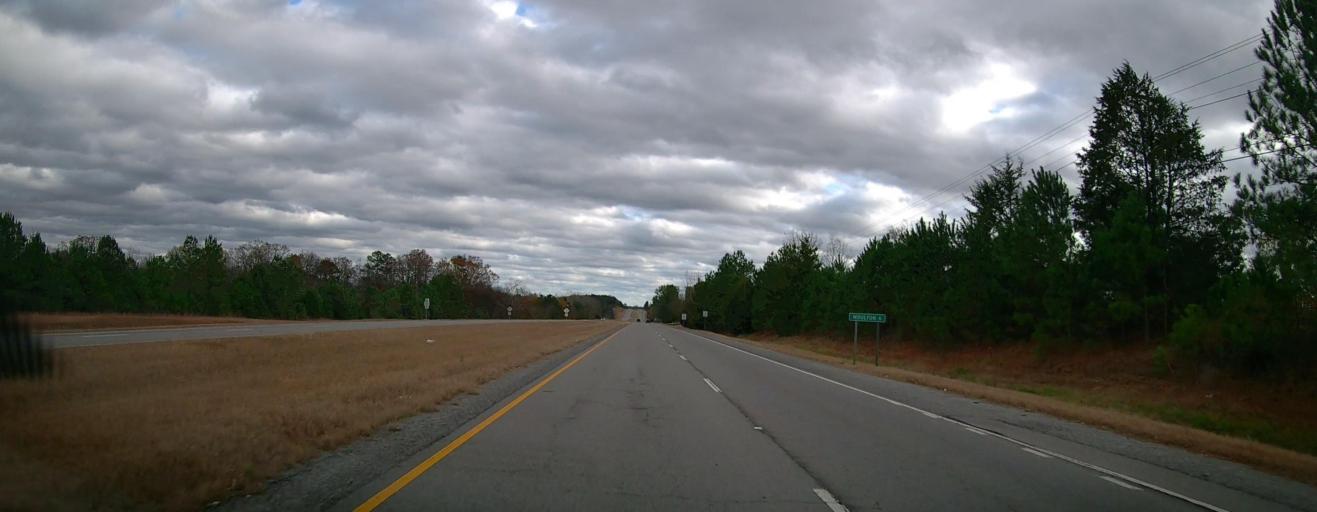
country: US
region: Alabama
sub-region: Lawrence County
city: Town Creek
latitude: 34.5877
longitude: -87.4221
